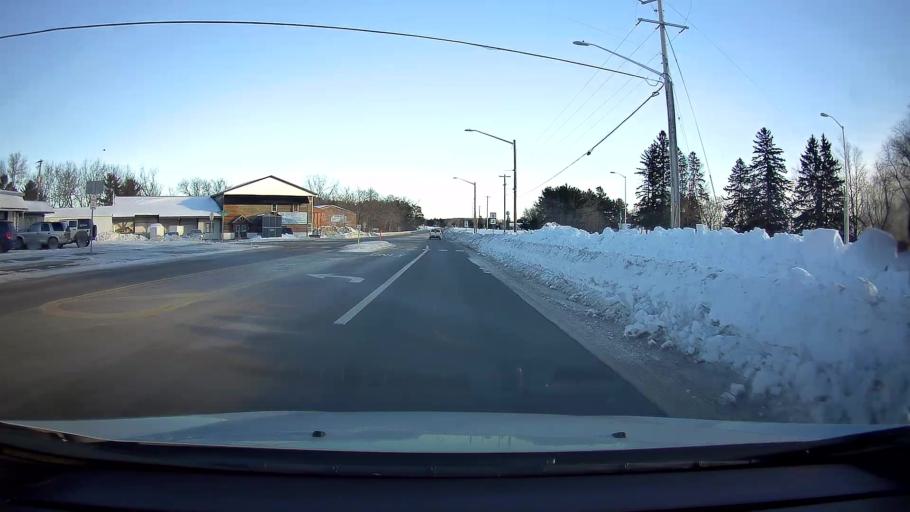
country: US
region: Wisconsin
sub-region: Washburn County
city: Shell Lake
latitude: 45.7435
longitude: -91.9230
